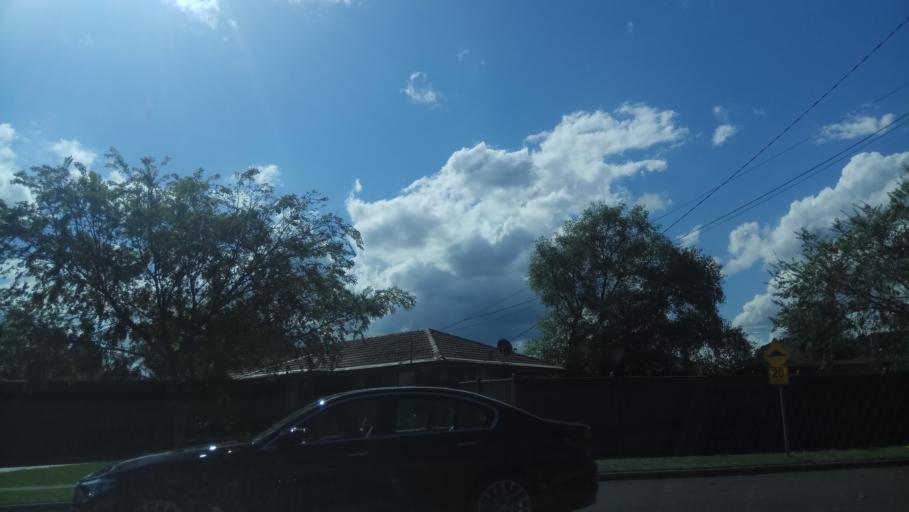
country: AU
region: Victoria
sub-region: Kingston
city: Dingley Village
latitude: -37.9812
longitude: 145.1251
